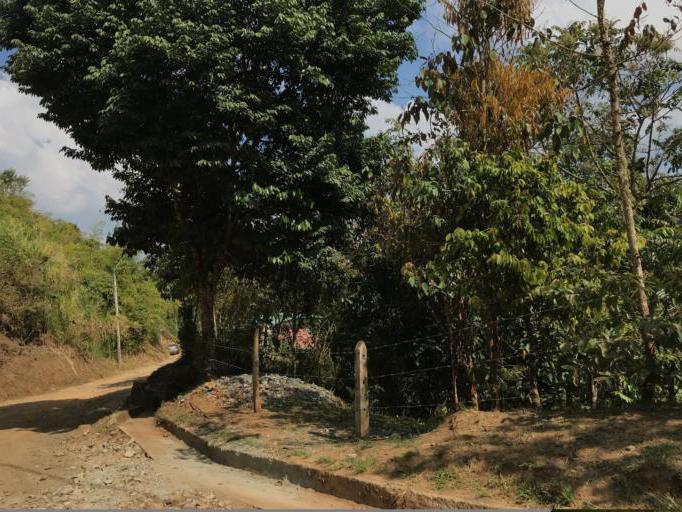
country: CO
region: Valle del Cauca
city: Cali
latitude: 3.4658
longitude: -76.6335
